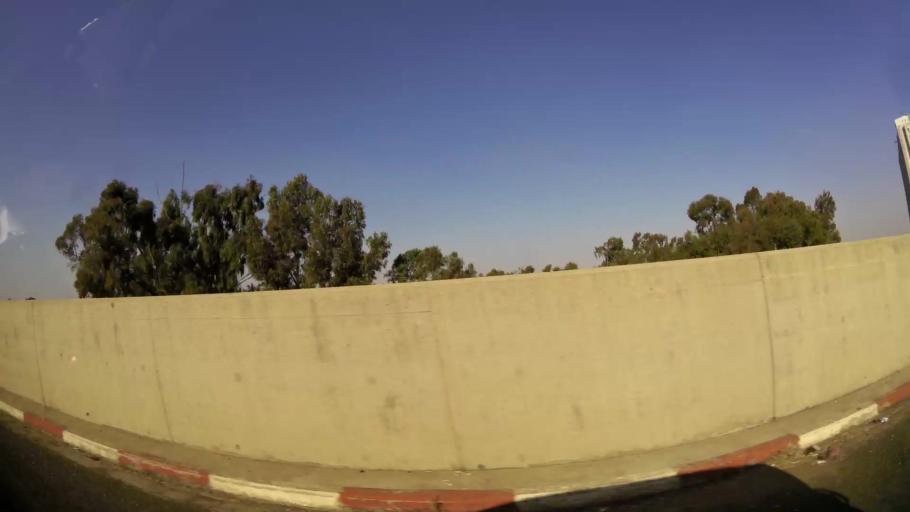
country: ZA
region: Gauteng
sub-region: West Rand District Municipality
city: Randfontein
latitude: -26.1628
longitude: 27.7133
